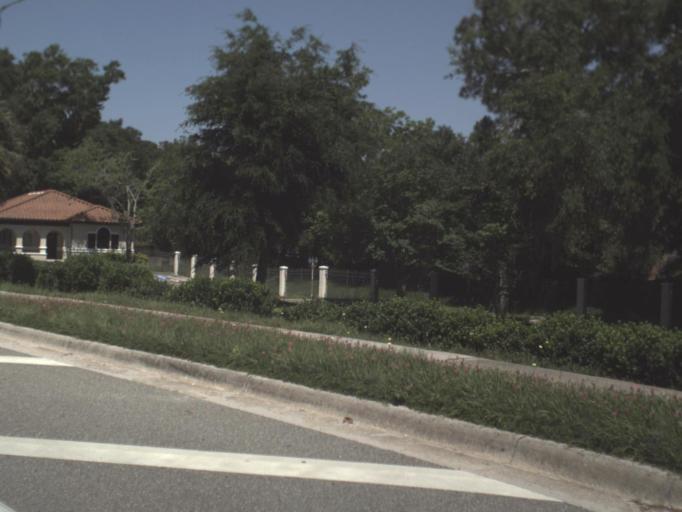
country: US
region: Florida
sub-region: Columbia County
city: Lake City
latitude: 30.1892
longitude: -82.6490
